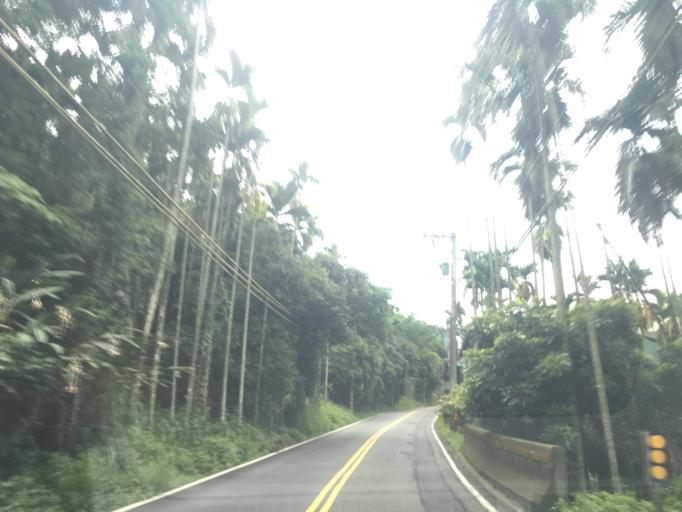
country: TW
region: Taiwan
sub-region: Yunlin
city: Douliu
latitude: 23.5677
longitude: 120.5703
